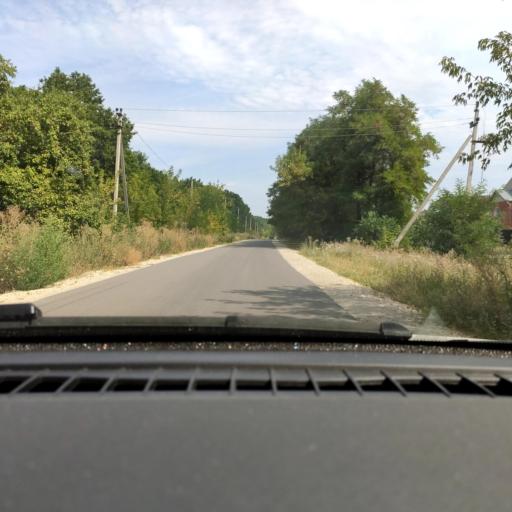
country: RU
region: Voronezj
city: Pridonskoy
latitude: 51.7354
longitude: 39.0626
